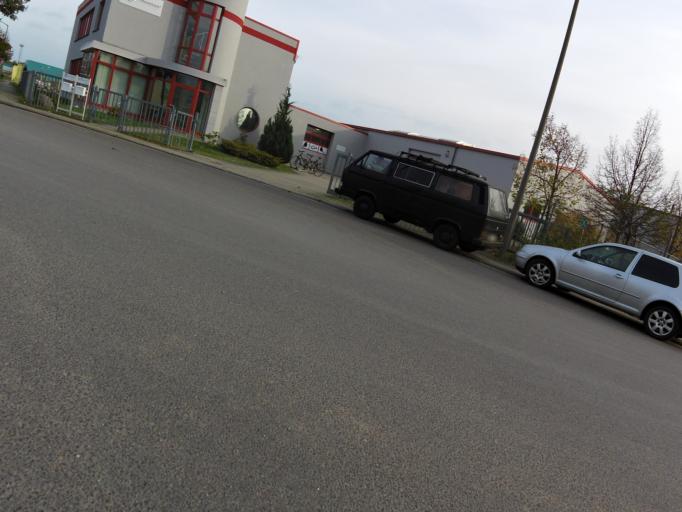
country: DE
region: Saxony
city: Taucha
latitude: 51.3644
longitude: 12.4366
